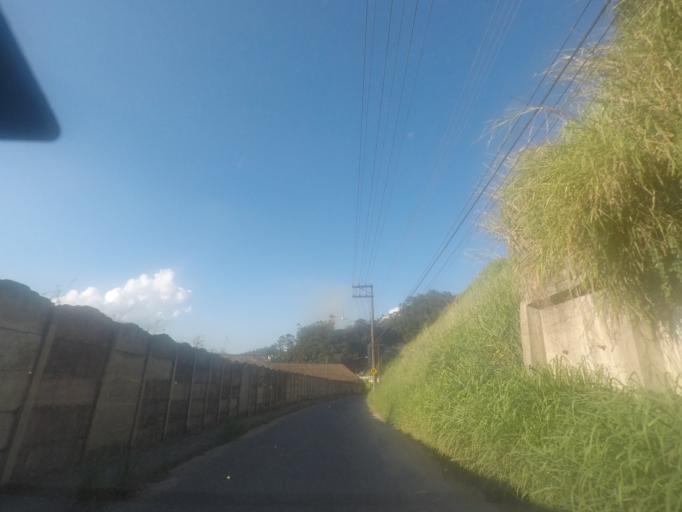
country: BR
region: Rio de Janeiro
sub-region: Petropolis
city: Petropolis
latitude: -22.4891
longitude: -43.1510
